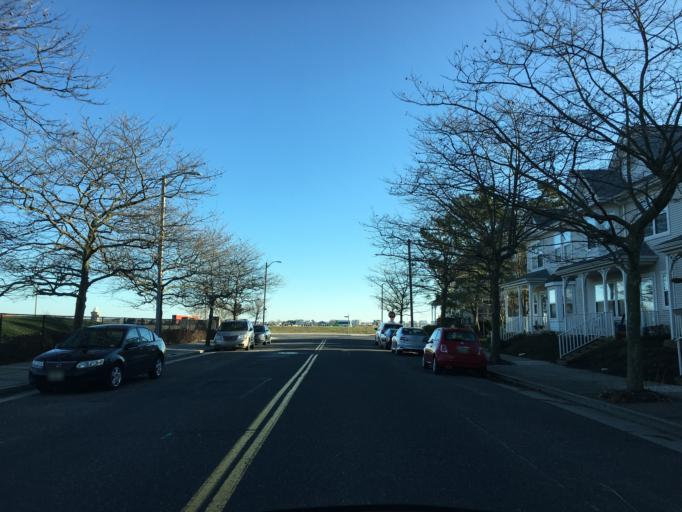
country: US
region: New Jersey
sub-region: Atlantic County
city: Atlantic City
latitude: 39.3757
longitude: -74.4190
